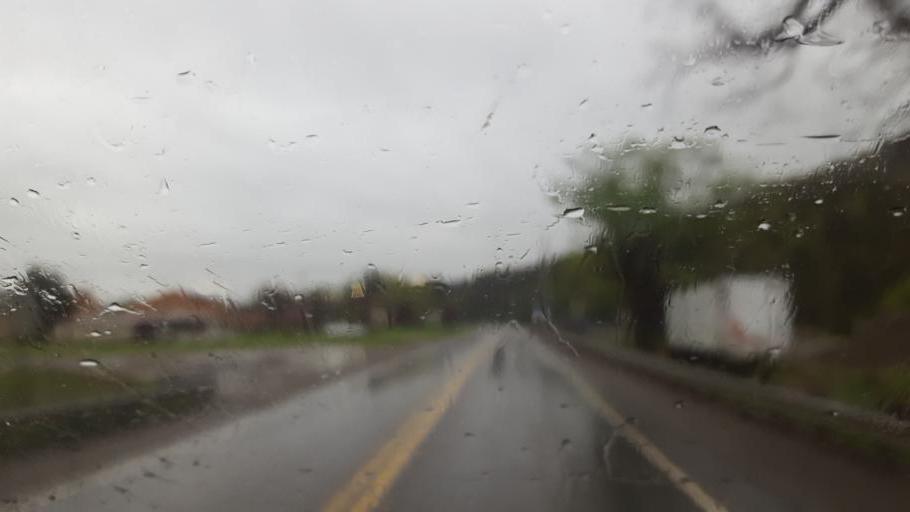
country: US
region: Pennsylvania
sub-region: Tioga County
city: Westfield
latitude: 41.9176
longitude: -77.5580
